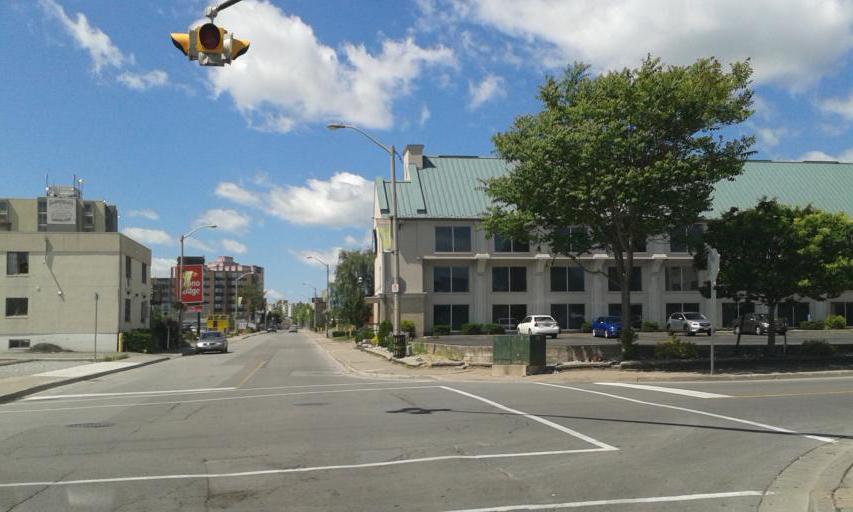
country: CA
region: Ontario
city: Niagara Falls
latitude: 43.0928
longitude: -79.0771
